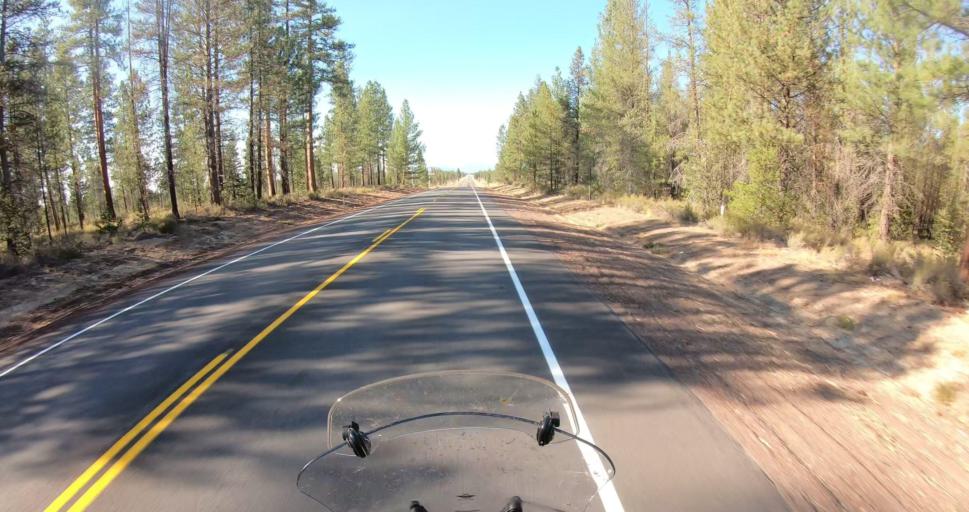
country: US
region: Oregon
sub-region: Deschutes County
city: La Pine
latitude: 43.5593
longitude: -121.4761
